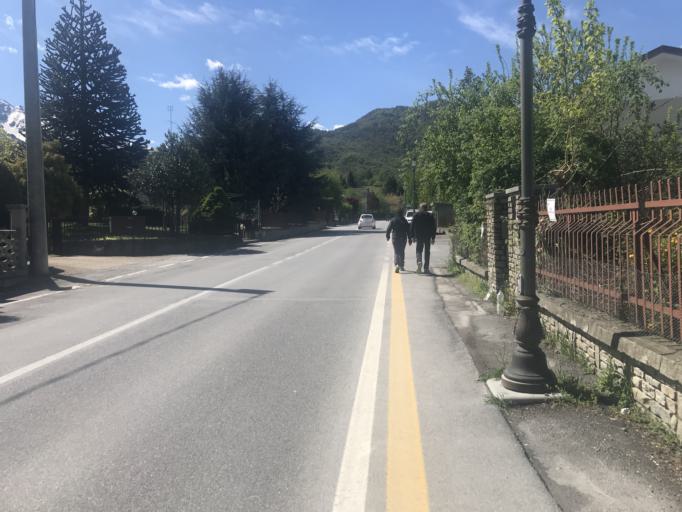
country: IT
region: Piedmont
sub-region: Provincia di Cuneo
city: Boves
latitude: 44.3255
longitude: 7.5548
